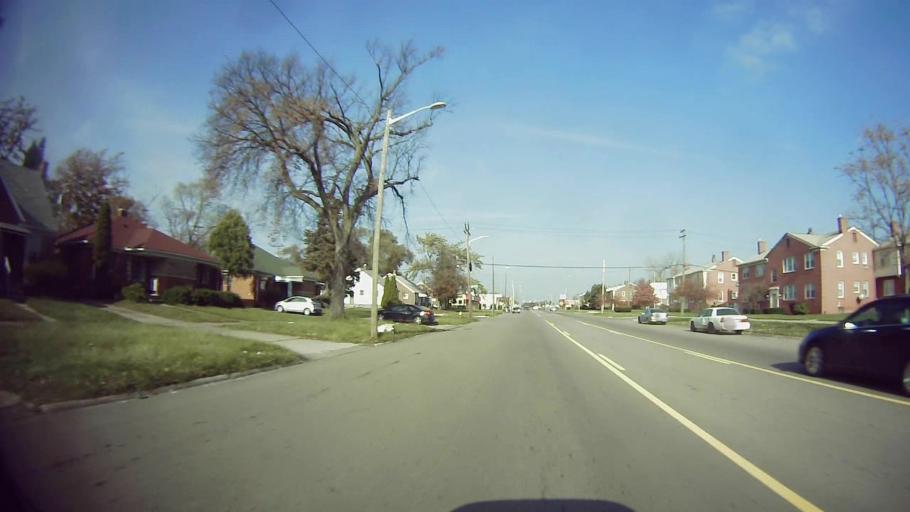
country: US
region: Michigan
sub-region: Oakland County
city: Oak Park
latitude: 42.4393
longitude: -83.1809
